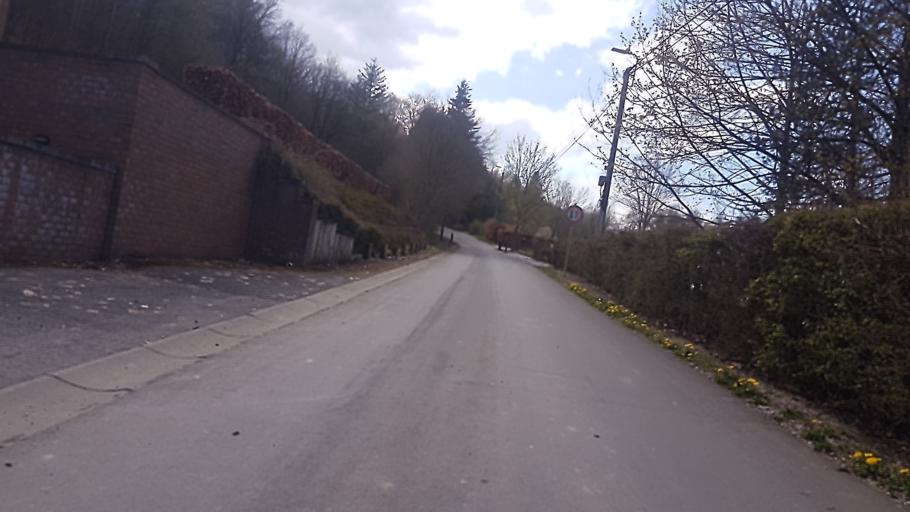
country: BE
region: Wallonia
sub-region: Province de Namur
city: Couvin
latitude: 50.0713
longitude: 4.6011
